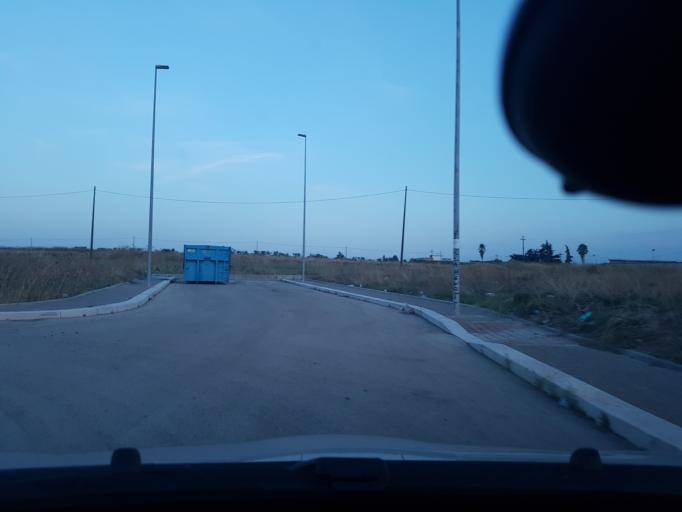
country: IT
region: Apulia
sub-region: Provincia di Foggia
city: Cerignola
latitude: 41.2588
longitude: 15.8768
